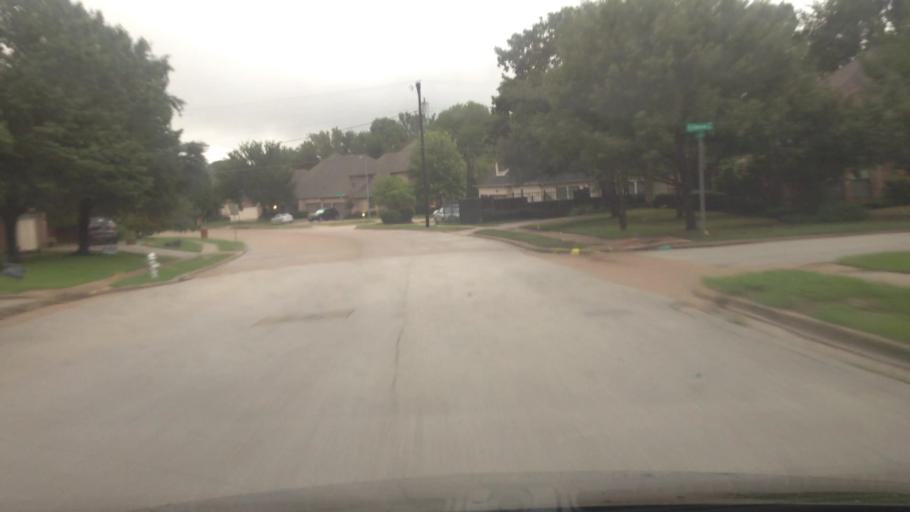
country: US
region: Texas
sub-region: Tarrant County
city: Colleyville
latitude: 32.8778
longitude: -97.1792
